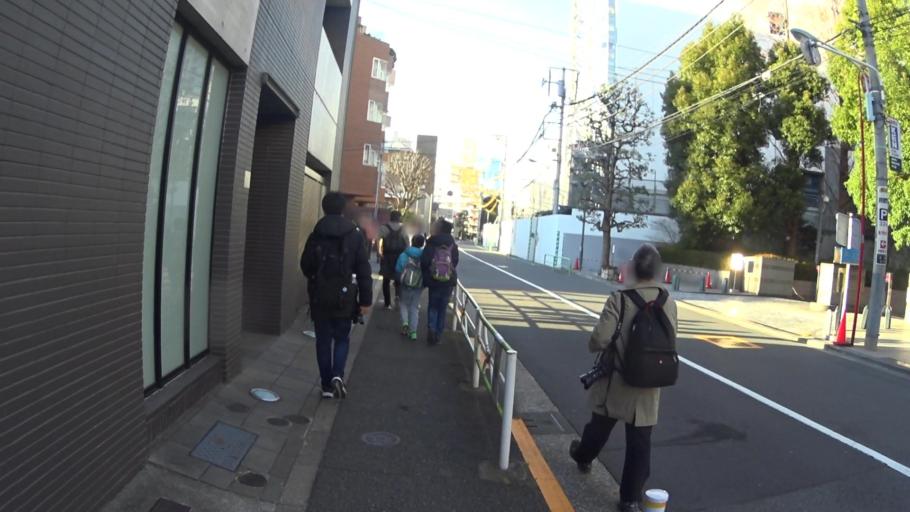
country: JP
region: Tokyo
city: Tokyo
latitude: 35.6721
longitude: 139.7329
